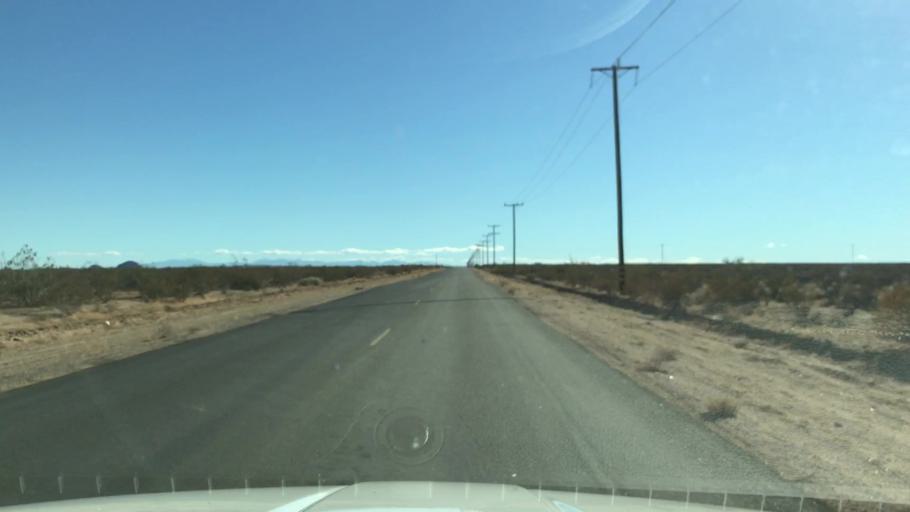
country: US
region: California
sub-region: Kern County
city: California City
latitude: 35.1884
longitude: -117.9858
